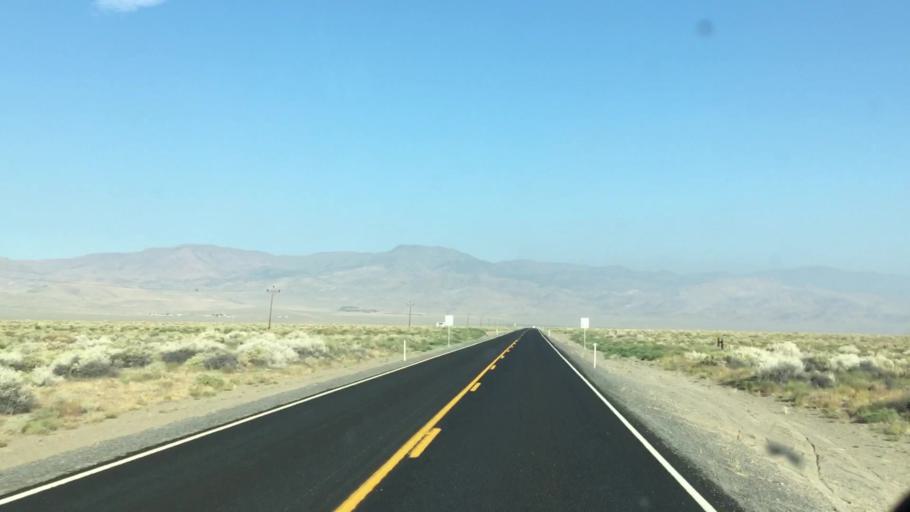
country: US
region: Nevada
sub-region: Lyon County
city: Fernley
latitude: 39.6424
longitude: -119.3026
